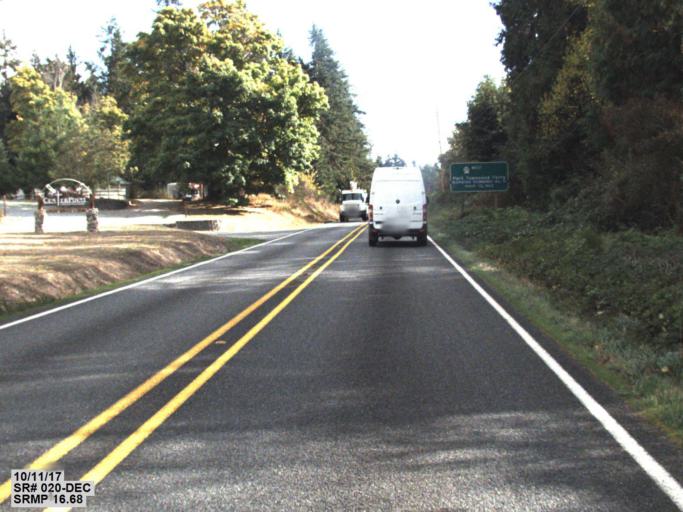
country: US
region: Washington
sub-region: Island County
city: Coupeville
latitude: 48.1741
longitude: -122.6140
